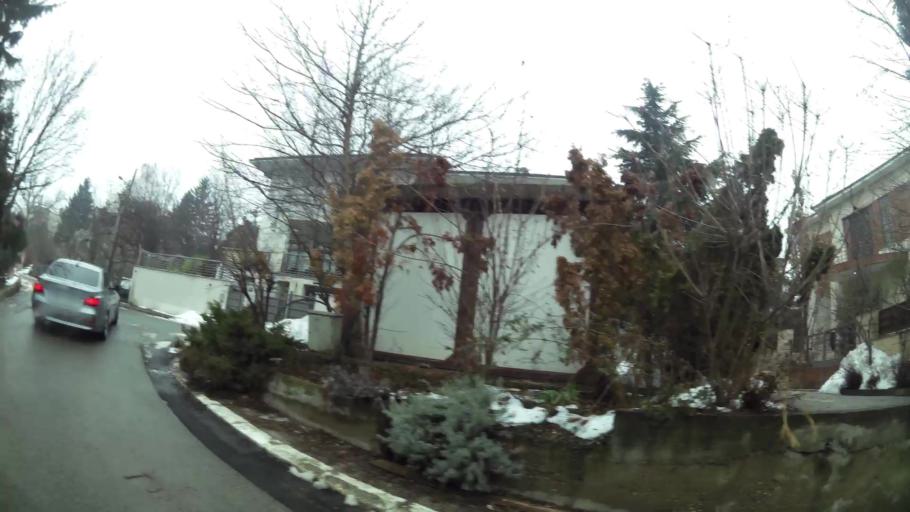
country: RS
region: Central Serbia
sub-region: Belgrade
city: Savski Venac
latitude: 44.7834
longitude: 20.4481
